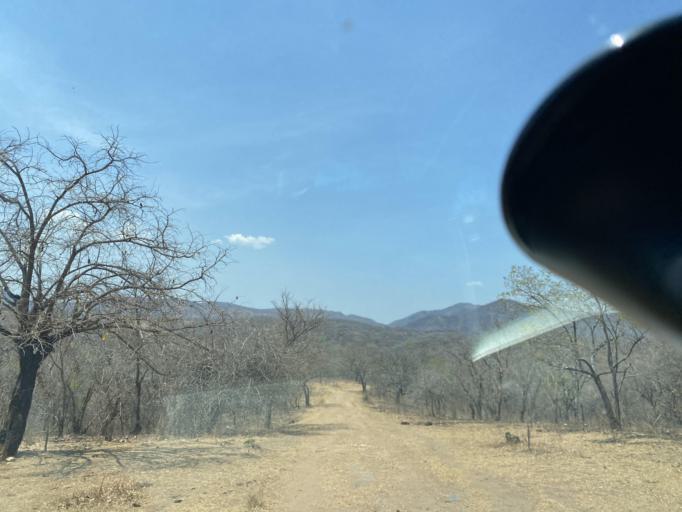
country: ZM
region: Lusaka
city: Kafue
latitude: -15.7884
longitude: 28.4575
